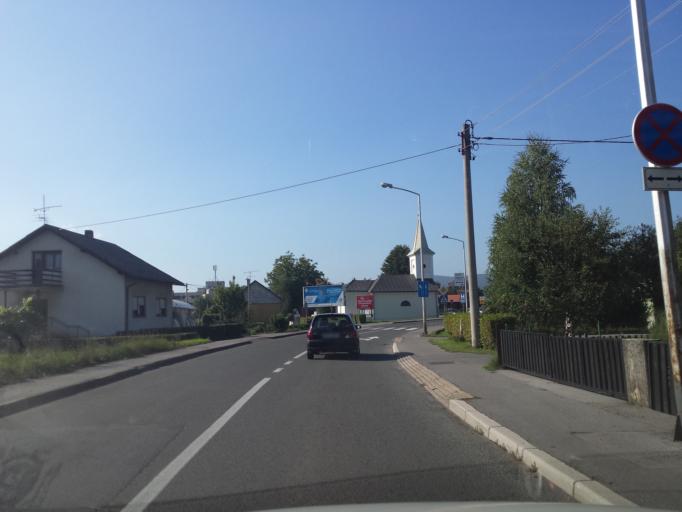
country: HR
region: Karlovacka
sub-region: Grad Ogulin
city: Ogulin
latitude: 45.2554
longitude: 15.2348
